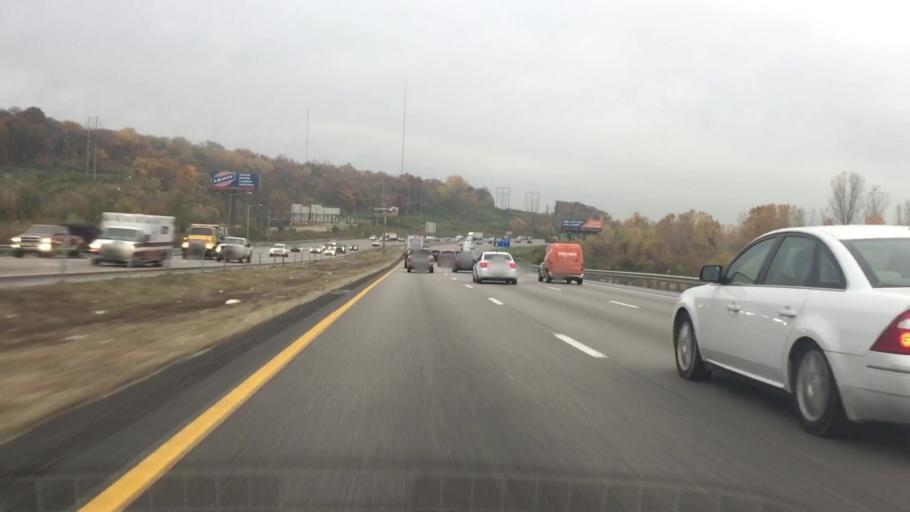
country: US
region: Missouri
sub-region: Jackson County
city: Sugar Creek
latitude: 39.0915
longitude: -94.4876
